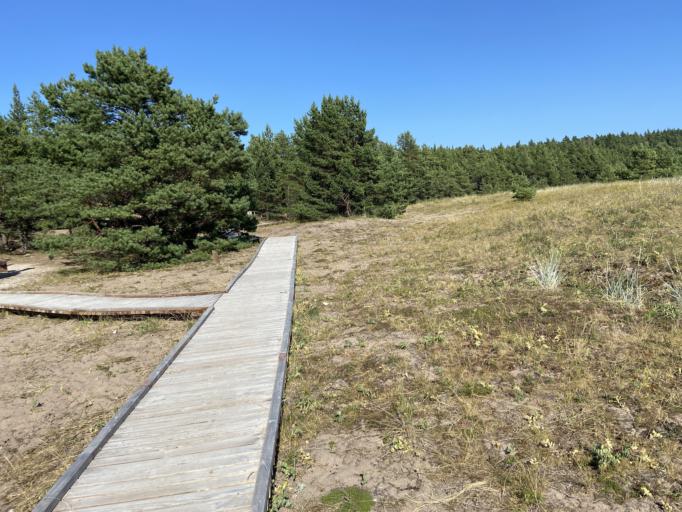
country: EE
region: Hiiumaa
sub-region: Kaerdla linn
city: Kardla
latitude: 58.9077
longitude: 22.1339
